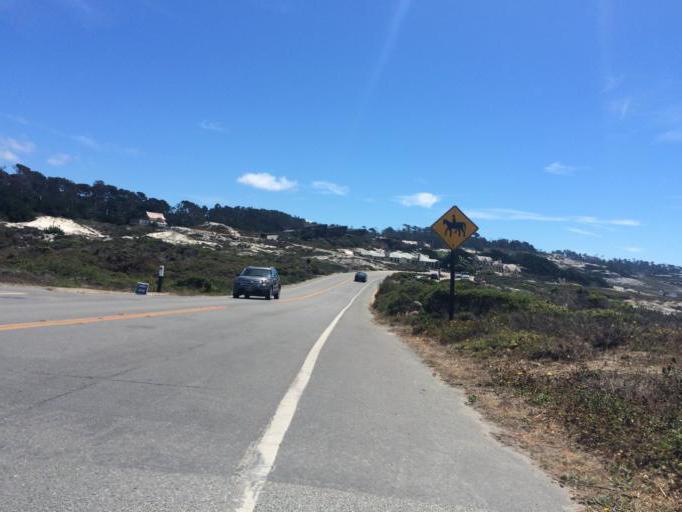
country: US
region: California
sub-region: Monterey County
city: Del Monte Forest
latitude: 36.5909
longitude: -121.9631
